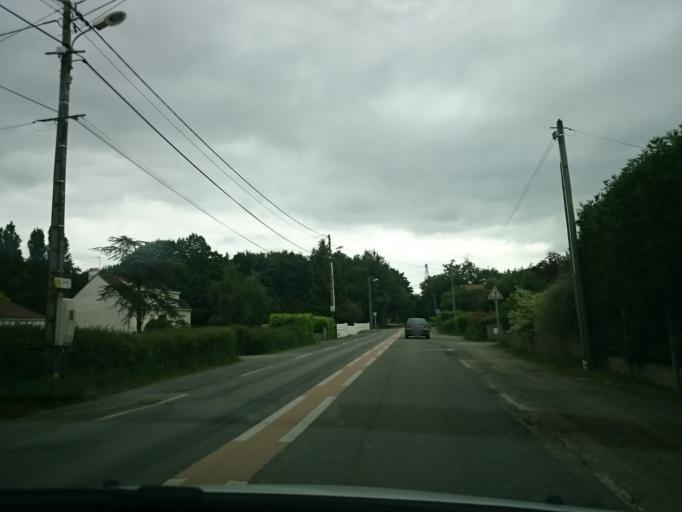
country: FR
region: Pays de la Loire
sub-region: Departement de la Loire-Atlantique
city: La Montagne
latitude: 47.1818
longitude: -1.6943
